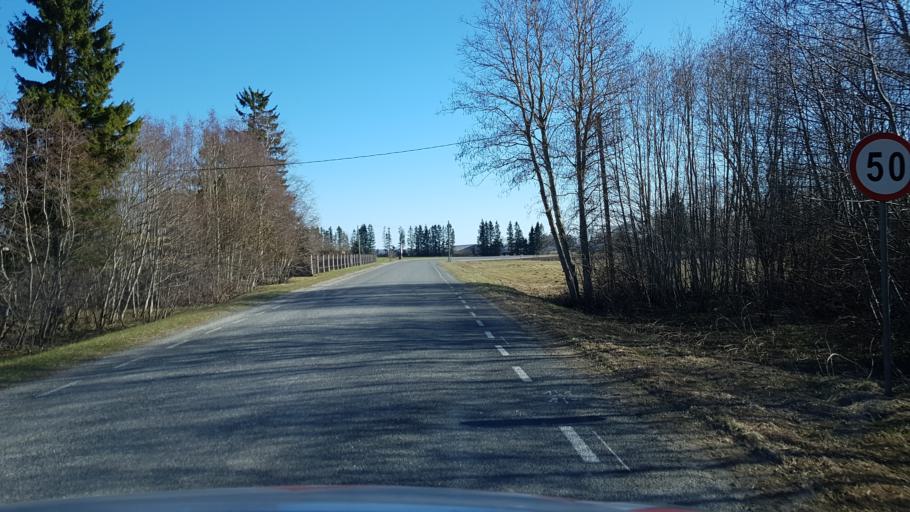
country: EE
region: Laeaene-Virumaa
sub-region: Someru vald
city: Someru
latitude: 59.3686
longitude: 26.4500
